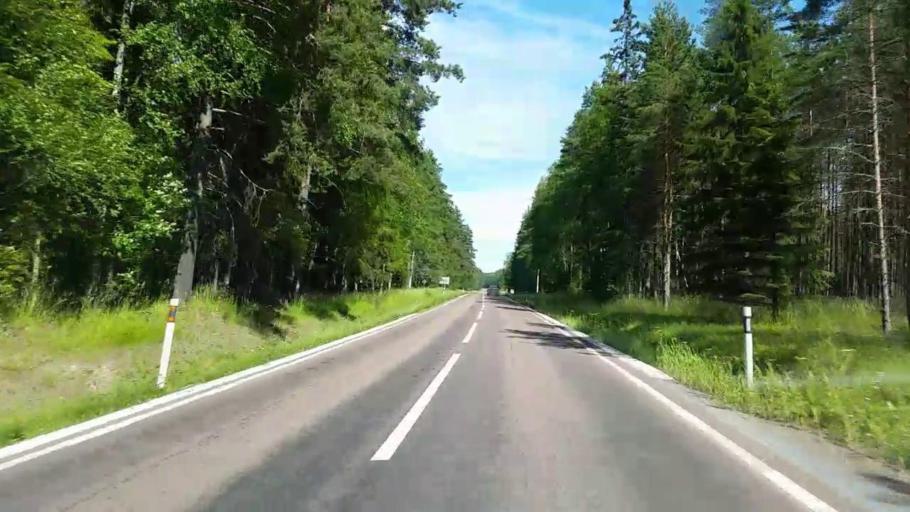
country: SE
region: Dalarna
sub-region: Rattviks Kommun
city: Raettvik
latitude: 60.9015
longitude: 15.1856
